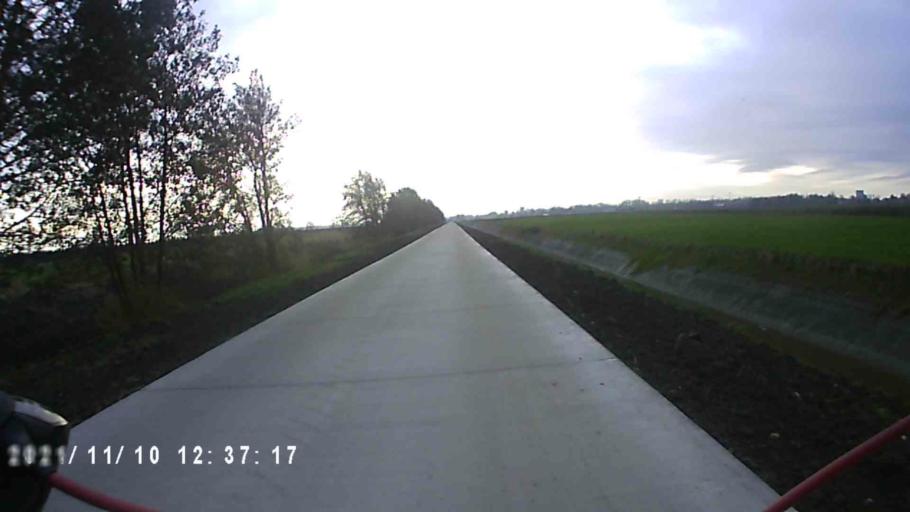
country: NL
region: Groningen
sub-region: Gemeente Groningen
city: Korrewegwijk
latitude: 53.2604
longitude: 6.5479
